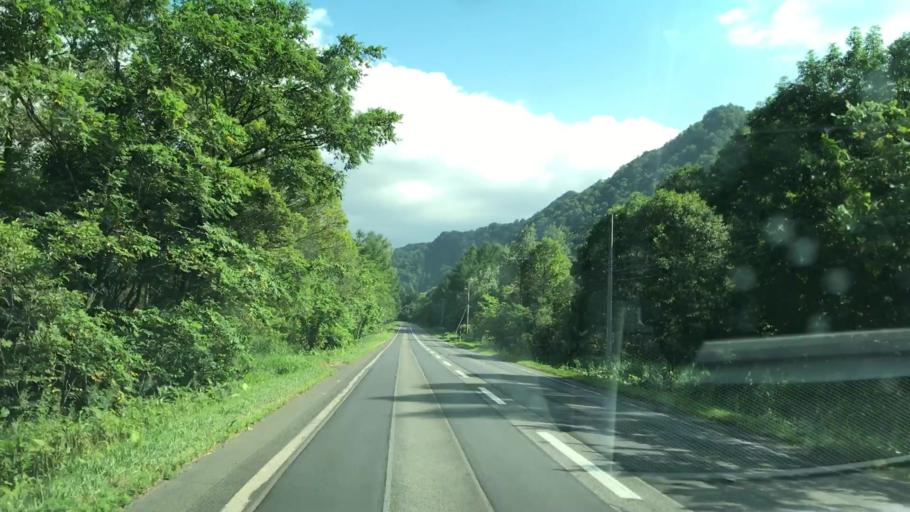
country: JP
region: Hokkaido
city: Shizunai-furukawacho
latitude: 42.8307
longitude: 142.4160
